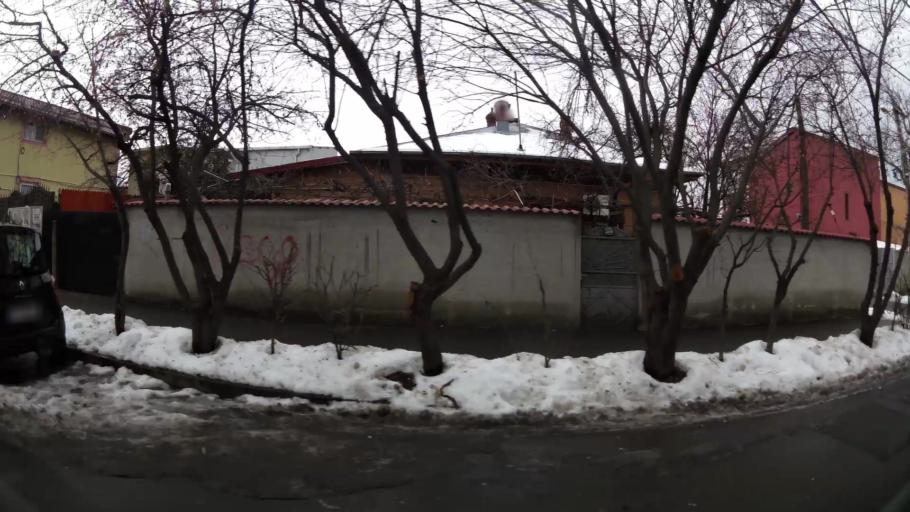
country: RO
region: Ilfov
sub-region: Comuna Pantelimon
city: Pantelimon
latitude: 44.4334
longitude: 26.1998
